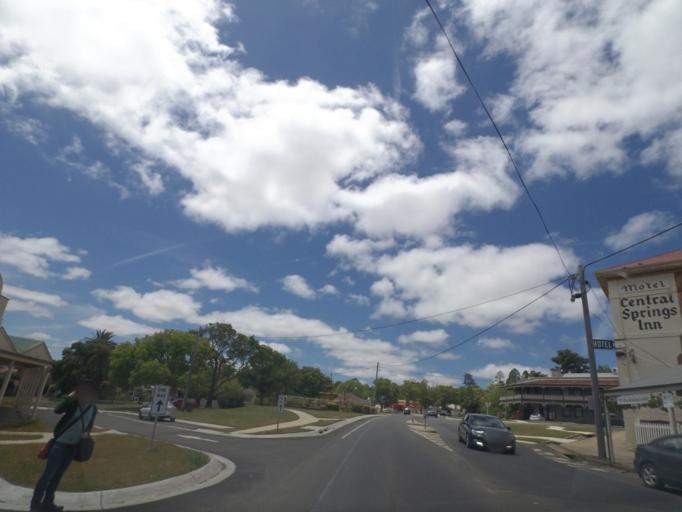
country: AU
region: Victoria
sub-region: Mount Alexander
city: Castlemaine
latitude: -37.3402
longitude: 144.1452
